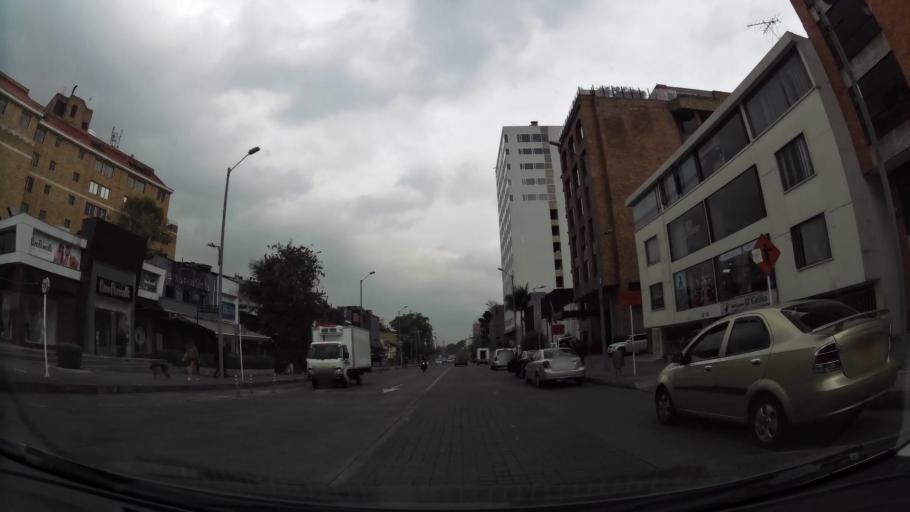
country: CO
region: Bogota D.C.
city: Barrio San Luis
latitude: 4.6685
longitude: -74.0524
